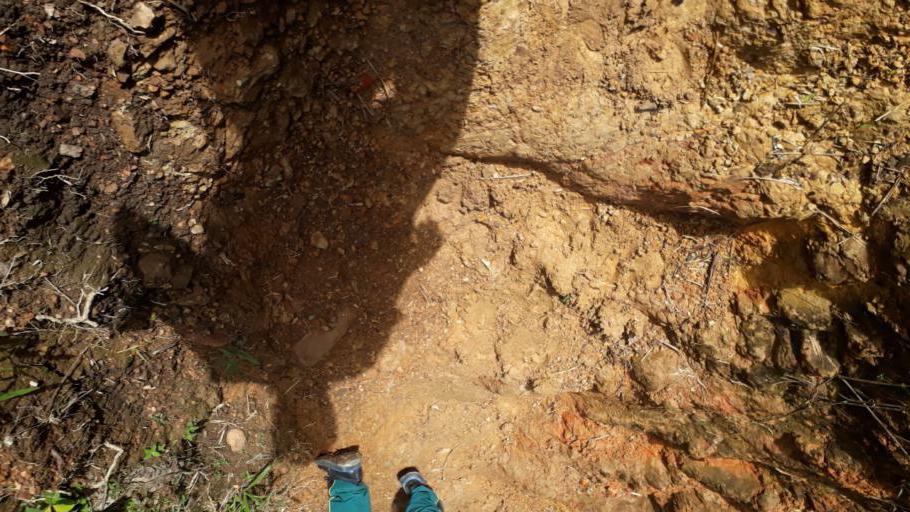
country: CO
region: Casanare
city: Nunchia
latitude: 5.6698
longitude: -72.4360
